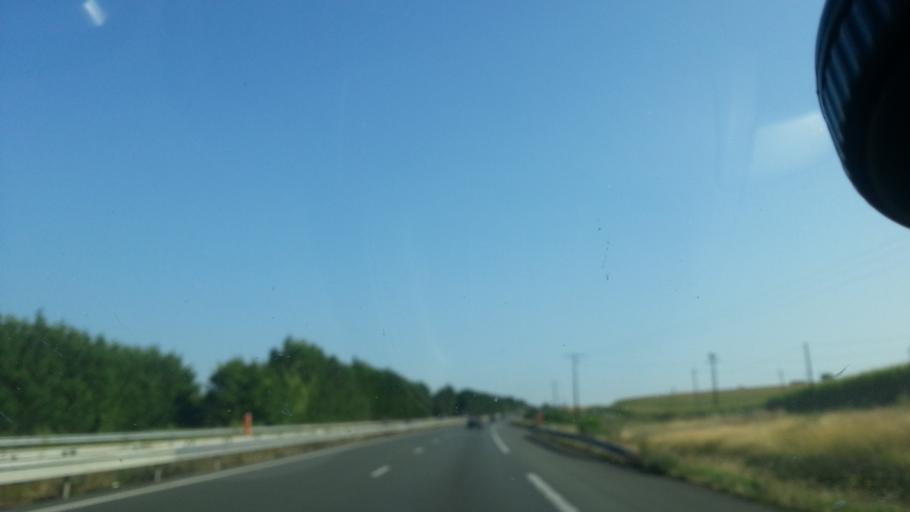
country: FR
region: Poitou-Charentes
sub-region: Departement de la Vienne
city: Antran
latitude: 46.8835
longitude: 0.5176
